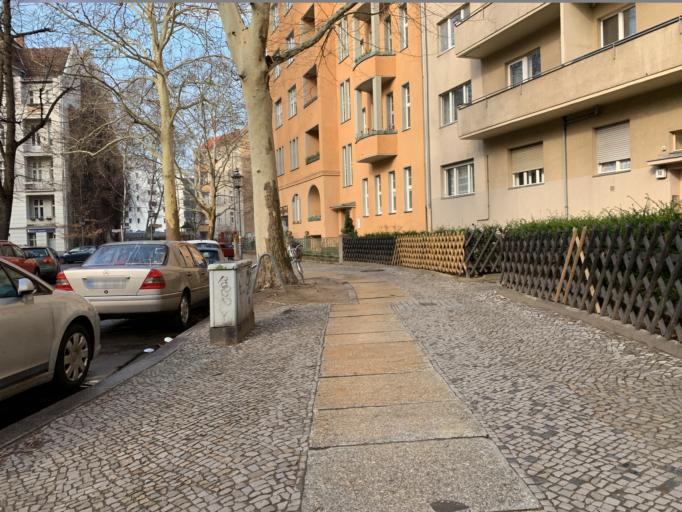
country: DE
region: Berlin
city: Charlottenburg-Nord
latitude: 52.5175
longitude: 13.3030
